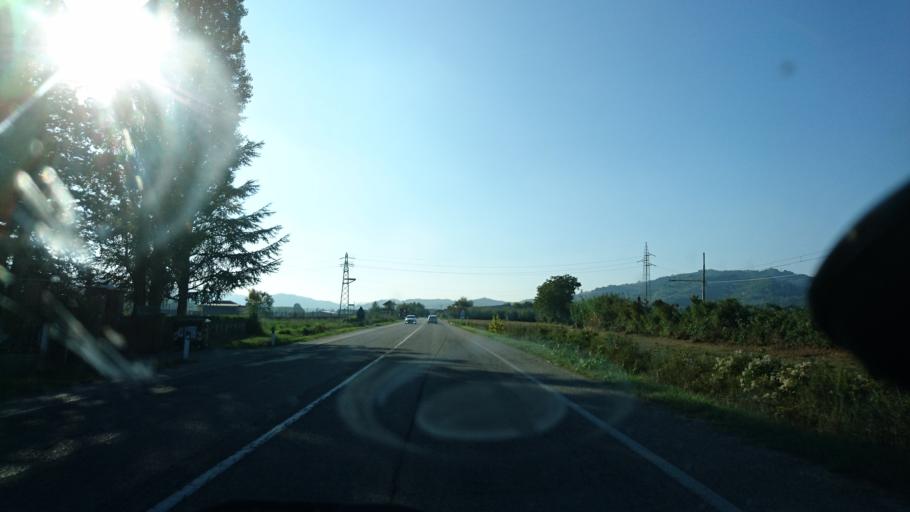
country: IT
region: Piedmont
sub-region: Provincia di Alessandria
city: Bistagno
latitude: 44.6582
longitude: 8.3840
